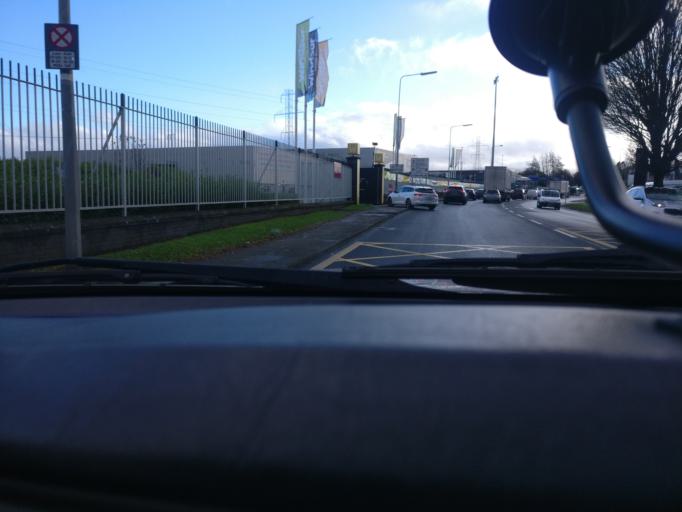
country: IE
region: Leinster
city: Crumlin
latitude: 53.3251
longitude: -6.3415
